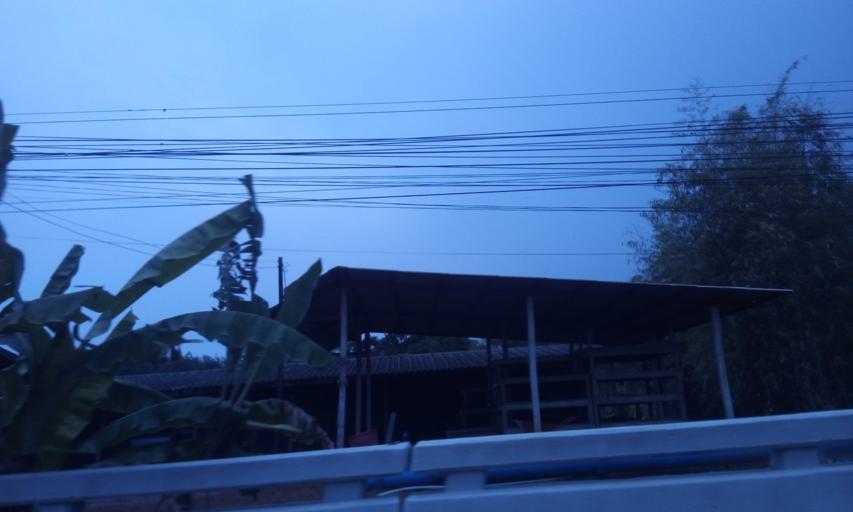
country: TH
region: Trat
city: Khao Saming
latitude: 12.3065
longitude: 102.3479
